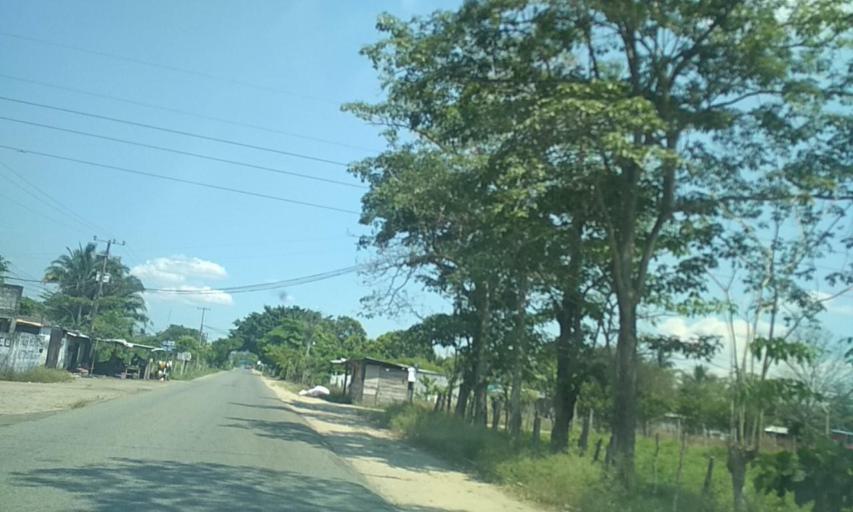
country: MX
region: Tabasco
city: Huimanguillo
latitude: 17.7934
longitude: -93.4442
